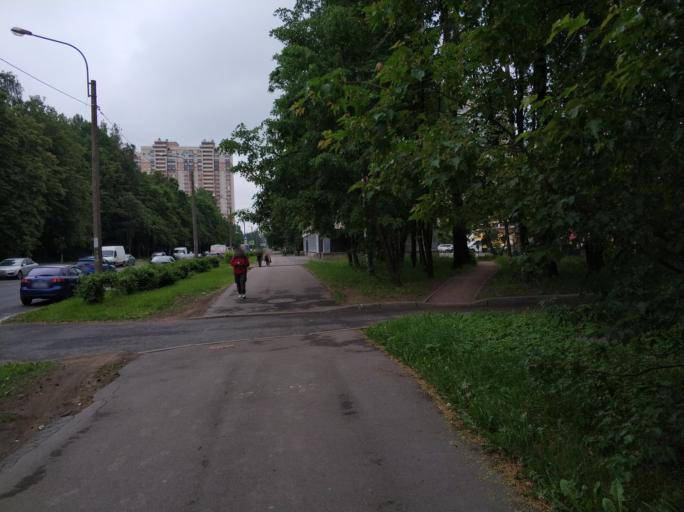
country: RU
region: St.-Petersburg
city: Grazhdanka
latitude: 60.0335
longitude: 30.3963
